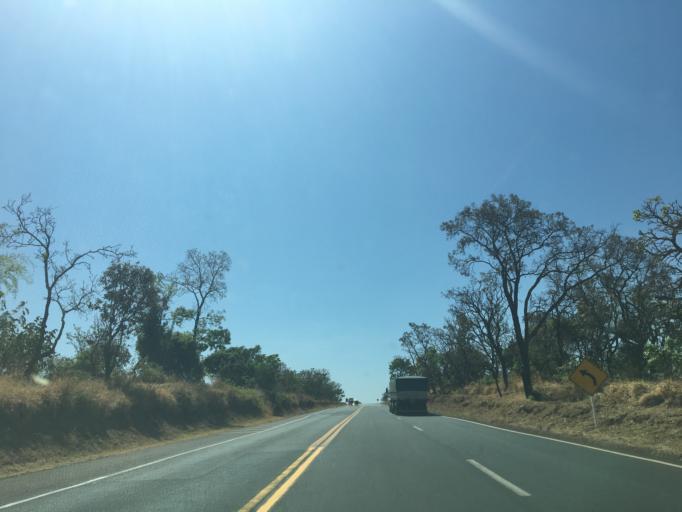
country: BR
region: Minas Gerais
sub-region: Monte Alegre De Minas
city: Monte Alegre de Minas
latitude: -18.9018
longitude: -49.0418
